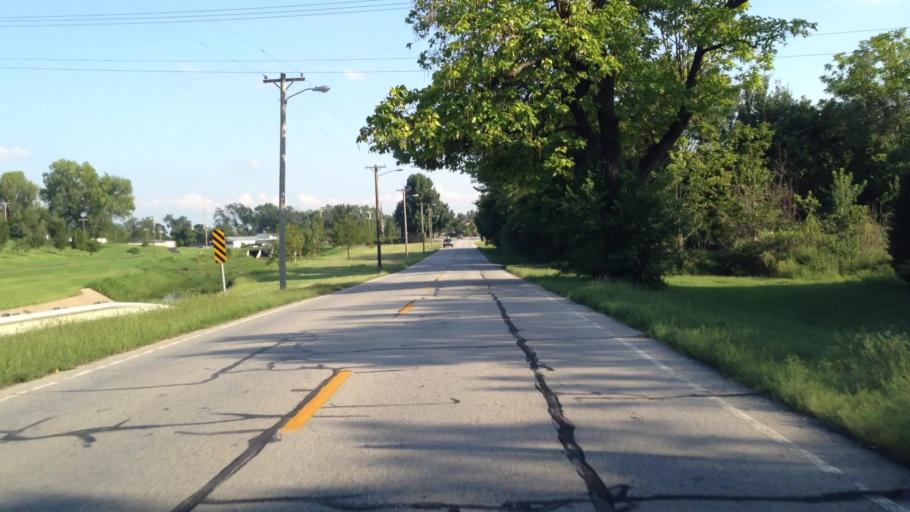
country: US
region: Missouri
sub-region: Jasper County
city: Joplin
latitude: 37.0903
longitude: -94.5086
